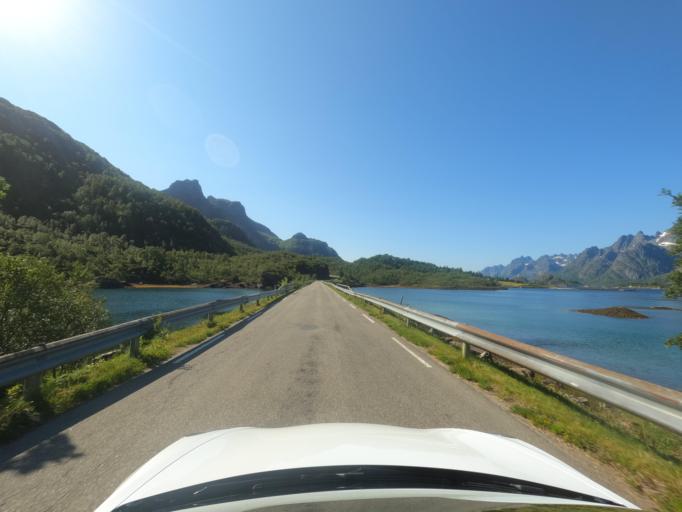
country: NO
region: Nordland
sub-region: Hadsel
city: Stokmarknes
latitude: 68.3556
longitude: 15.0728
